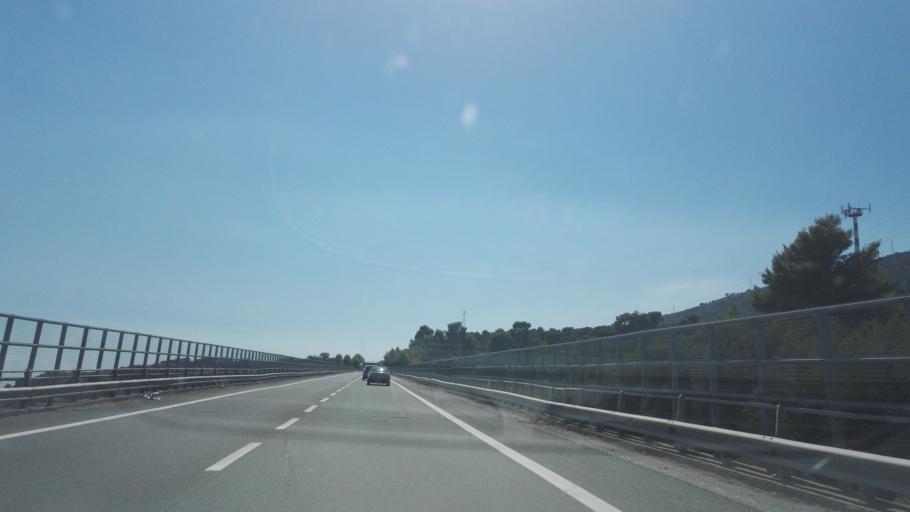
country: IT
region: Calabria
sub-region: Provincia di Cosenza
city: Trebisacce
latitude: 39.8790
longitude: 16.5385
